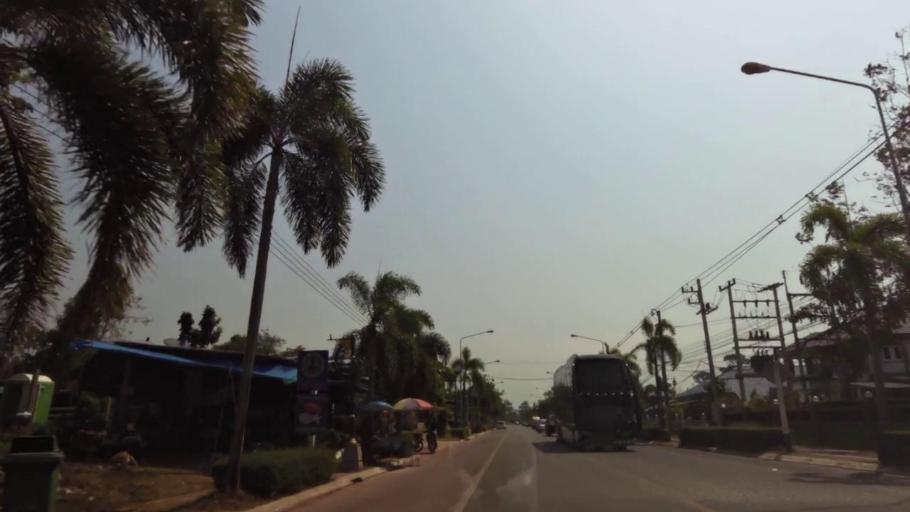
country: TH
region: Chanthaburi
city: Tha Mai
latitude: 12.5523
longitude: 101.9231
